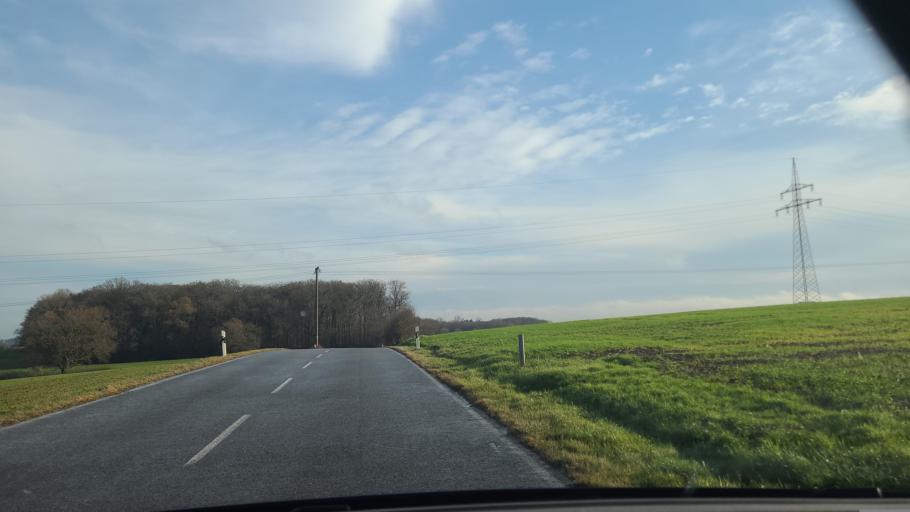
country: LU
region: Luxembourg
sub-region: Canton de Capellen
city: Koerich
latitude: 49.6522
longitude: 5.9627
